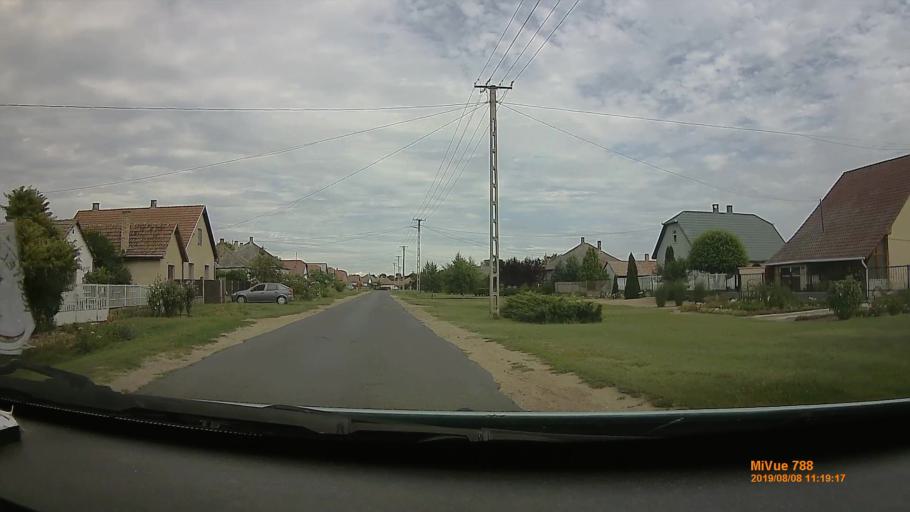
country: HU
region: Szabolcs-Szatmar-Bereg
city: Balkany
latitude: 47.7443
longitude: 21.8393
